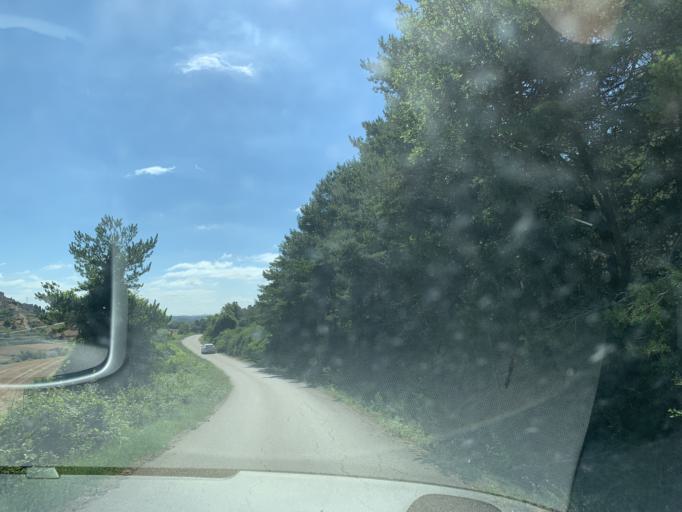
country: ES
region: Catalonia
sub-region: Provincia de Tarragona
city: Conesa
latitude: 41.5416
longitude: 1.2894
